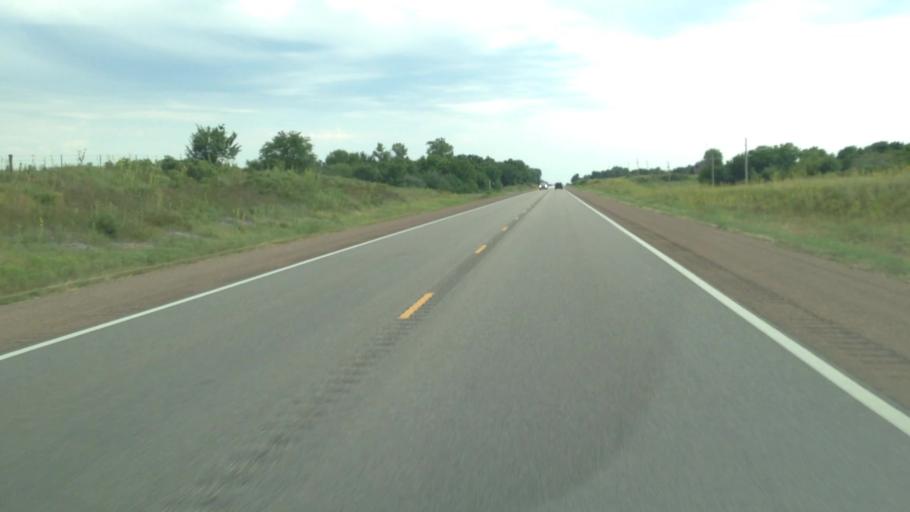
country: US
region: Kansas
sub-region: Woodson County
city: Yates Center
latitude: 37.9974
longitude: -95.7388
